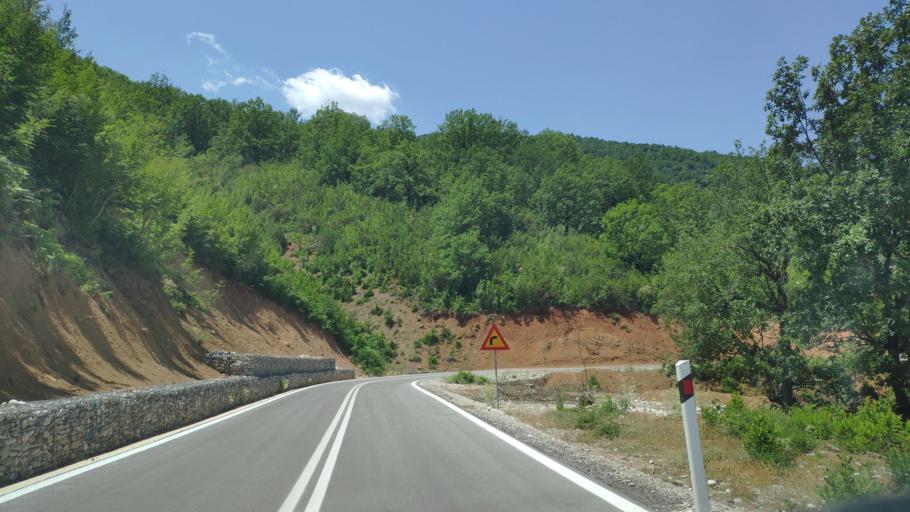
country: GR
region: Epirus
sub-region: Nomos Artas
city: Ano Kalentini
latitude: 39.1873
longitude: 21.3541
